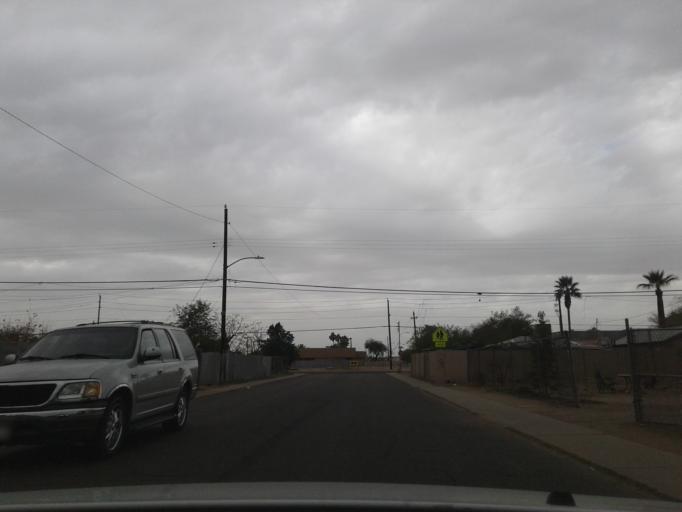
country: US
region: Arizona
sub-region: Maricopa County
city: Phoenix
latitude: 33.4474
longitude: -112.1250
